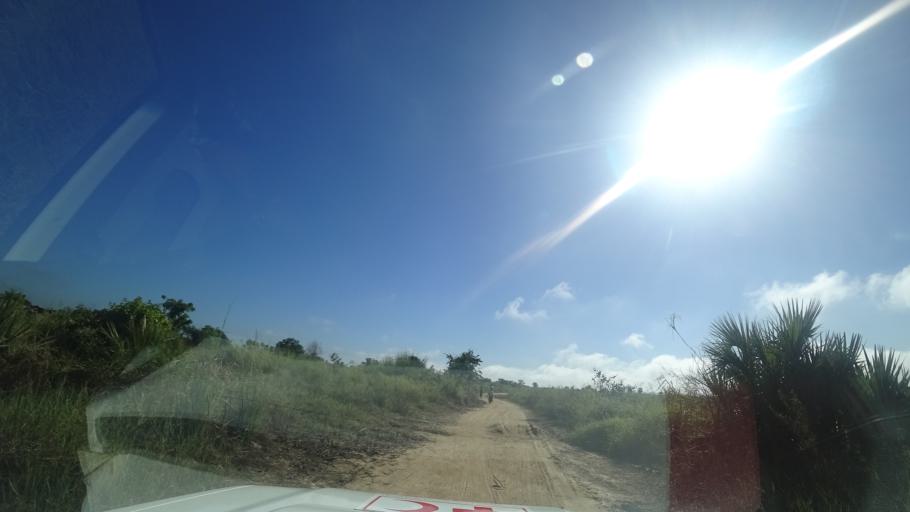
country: MZ
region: Sofala
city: Dondo
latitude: -19.4265
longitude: 34.5615
